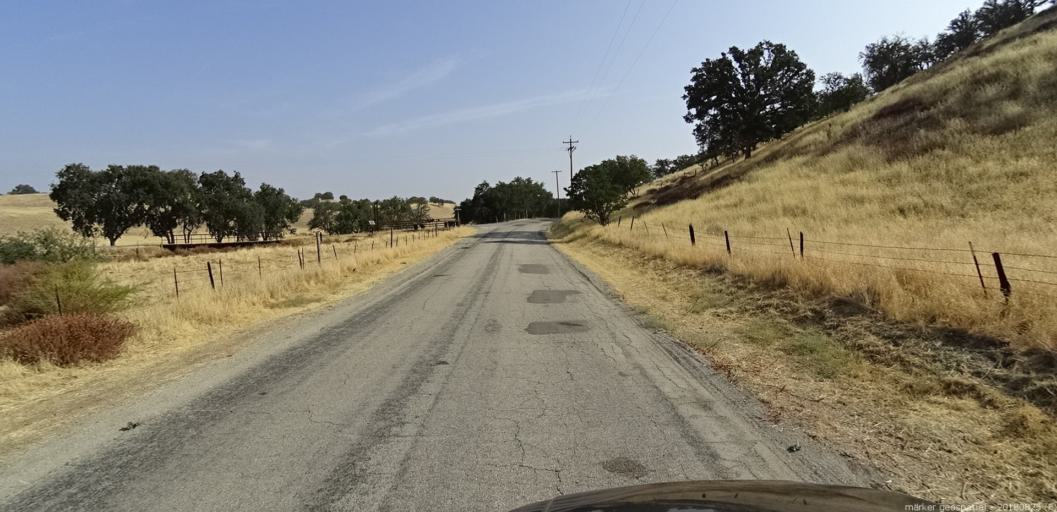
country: US
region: California
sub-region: San Luis Obispo County
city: San Miguel
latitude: 35.7535
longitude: -120.6090
